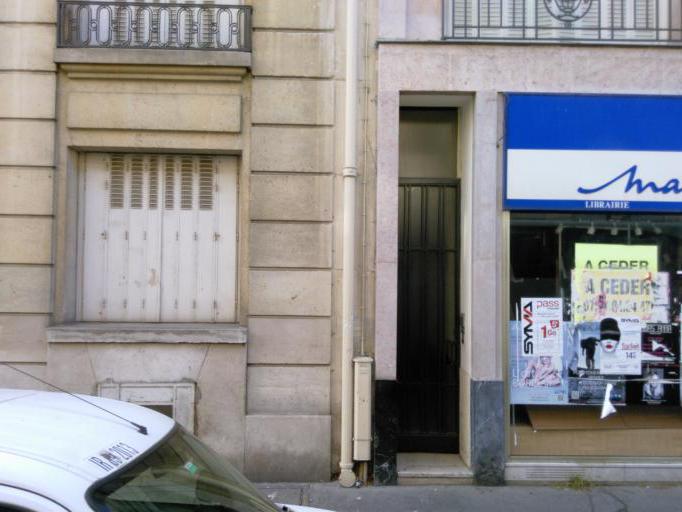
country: FR
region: Ile-de-France
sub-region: Departement des Hauts-de-Seine
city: Boulogne-Billancourt
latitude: 48.8493
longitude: 2.2670
